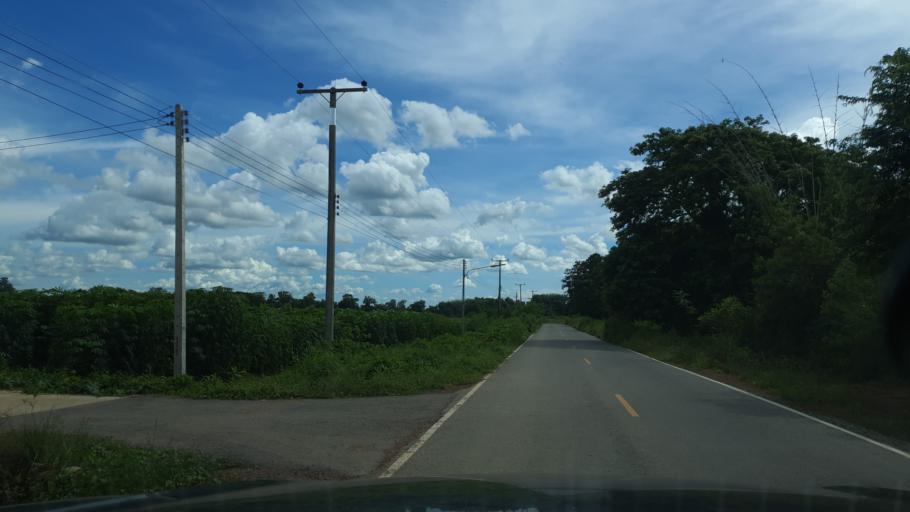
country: TH
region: Sukhothai
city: Thung Saliam
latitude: 17.3543
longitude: 99.6422
